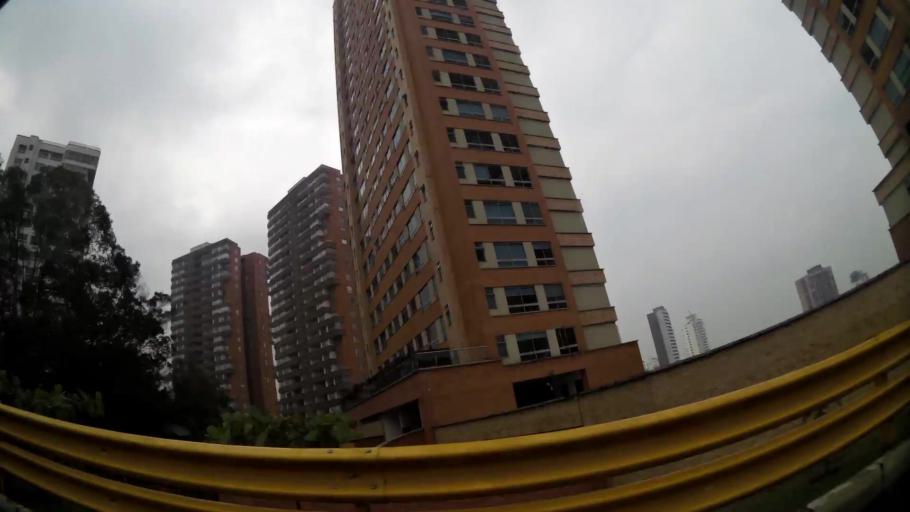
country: CO
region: Antioquia
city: Envigado
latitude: 6.1884
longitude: -75.5655
